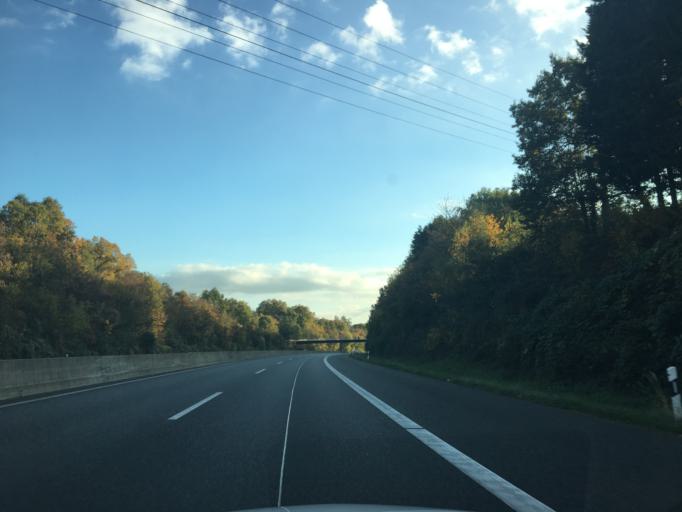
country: DE
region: Hesse
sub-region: Regierungsbezirk Darmstadt
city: Egelsbach
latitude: 49.9823
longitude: 8.6962
